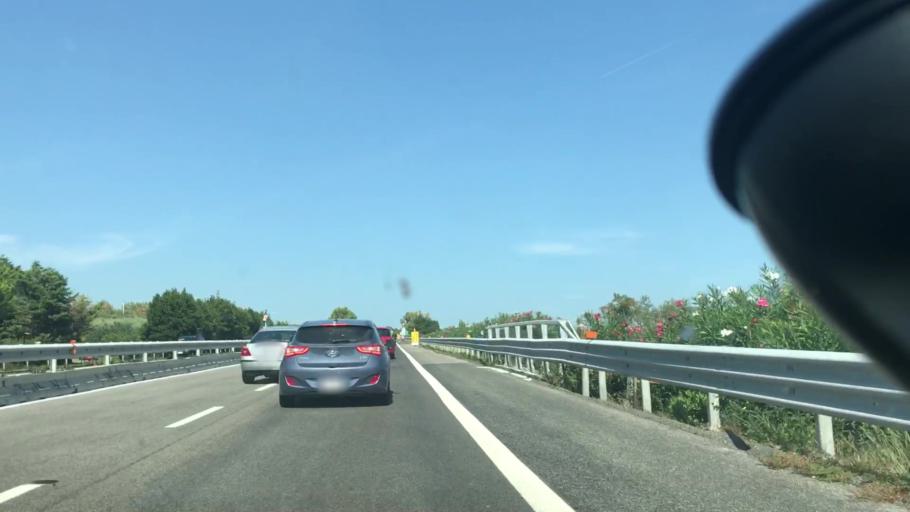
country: IT
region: Abruzzo
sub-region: Provincia di Chieti
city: San Salvo
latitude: 42.0658
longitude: 14.7279
